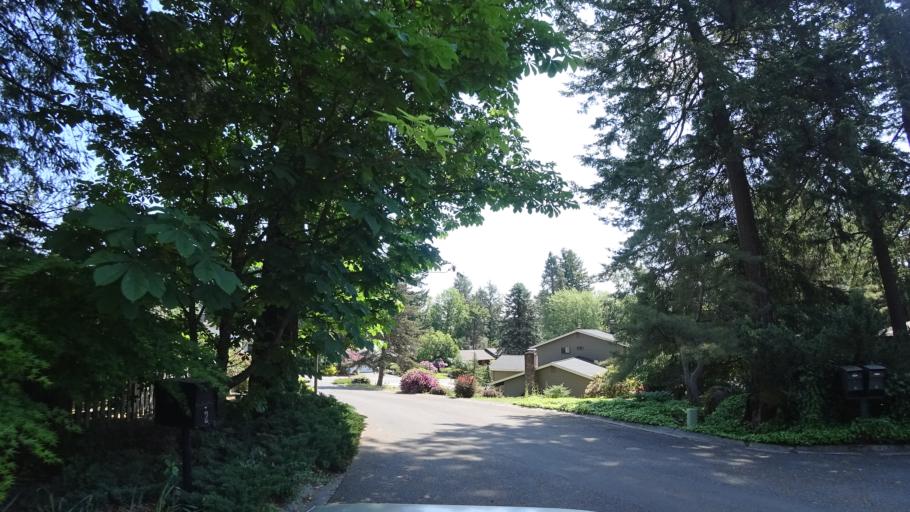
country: US
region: Oregon
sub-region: Clackamas County
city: Lake Oswego
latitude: 45.4325
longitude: -122.7091
